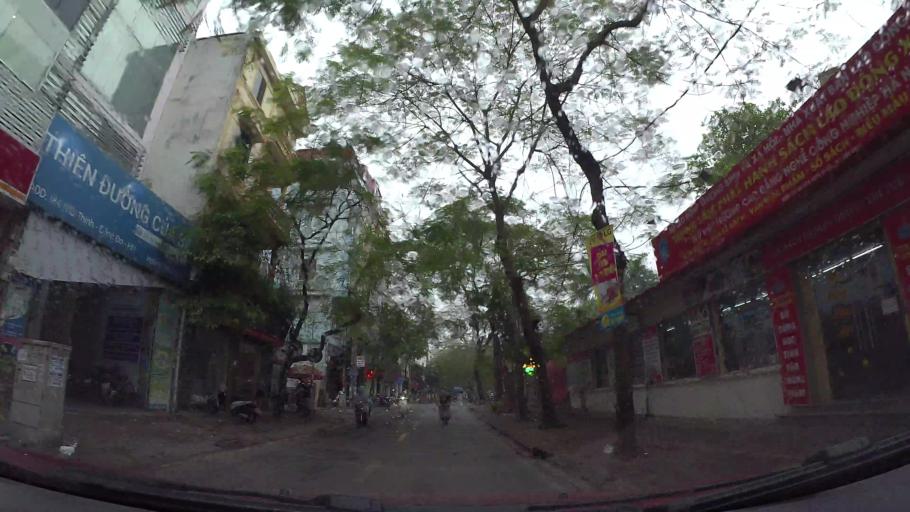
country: VN
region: Ha Noi
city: Dong Da
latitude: 21.0133
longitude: 105.8159
